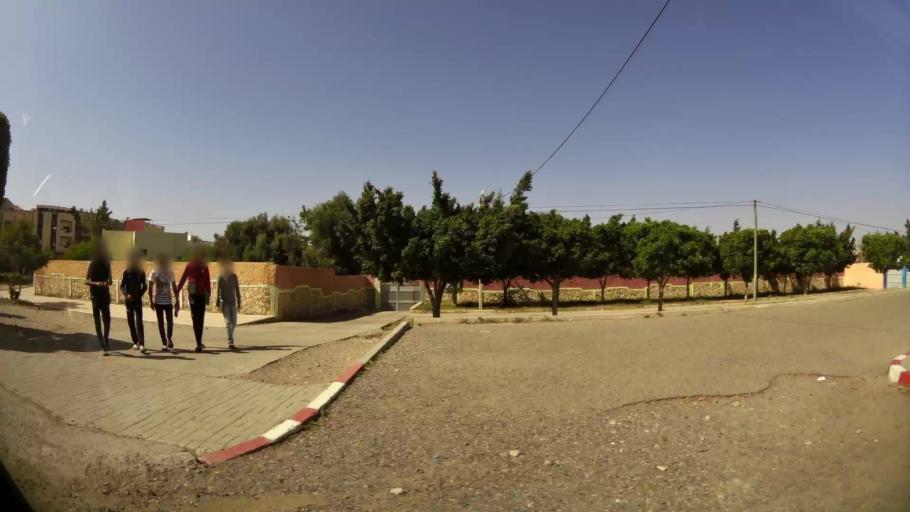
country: MA
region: Souss-Massa-Draa
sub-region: Inezgane-Ait Mellou
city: Inezgane
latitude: 30.3563
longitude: -9.5452
